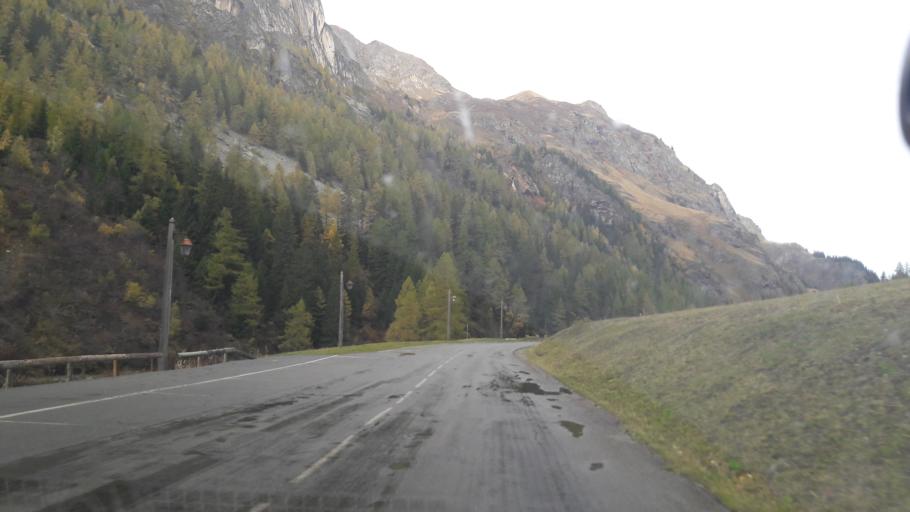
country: FR
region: Rhone-Alpes
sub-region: Departement de la Savoie
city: Tignes
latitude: 45.5116
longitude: 6.9169
